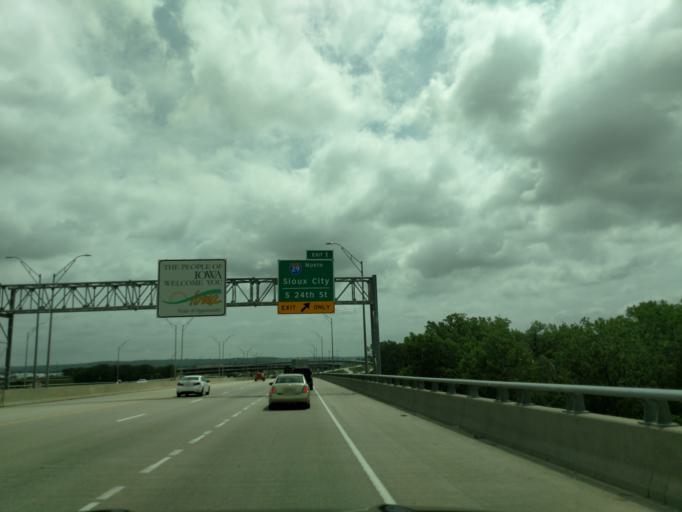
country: US
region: Nebraska
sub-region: Douglas County
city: Omaha
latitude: 41.2316
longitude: -95.9105
